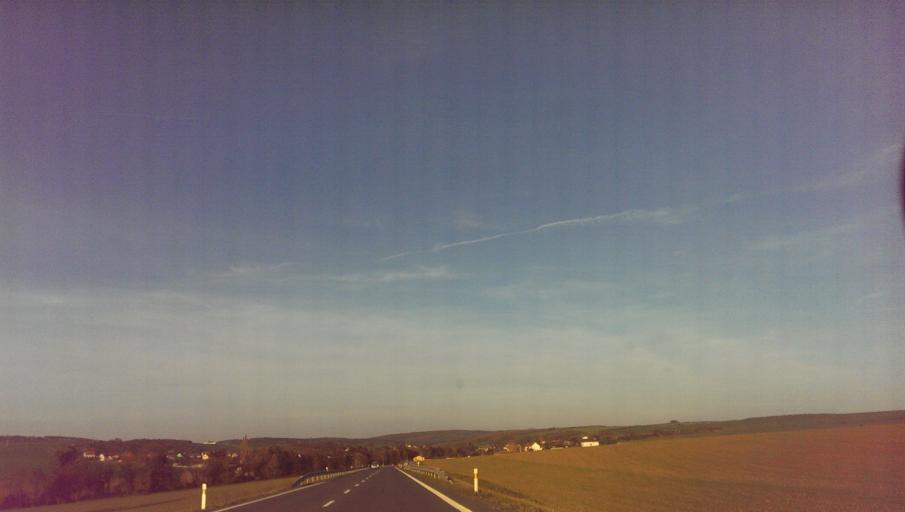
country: CZ
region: Zlin
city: Bilovice
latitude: 49.1108
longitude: 17.5645
